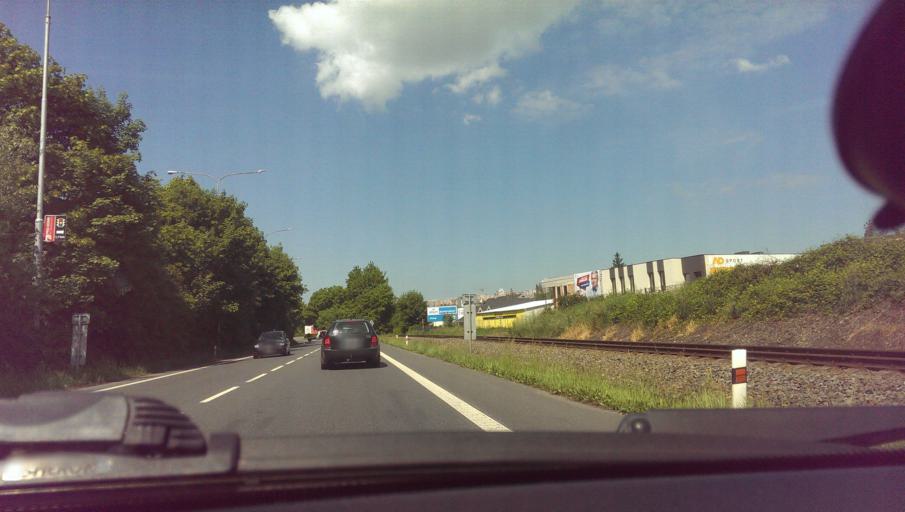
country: CZ
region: Zlin
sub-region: Okres Zlin
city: Zlin
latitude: 49.2241
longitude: 17.6991
